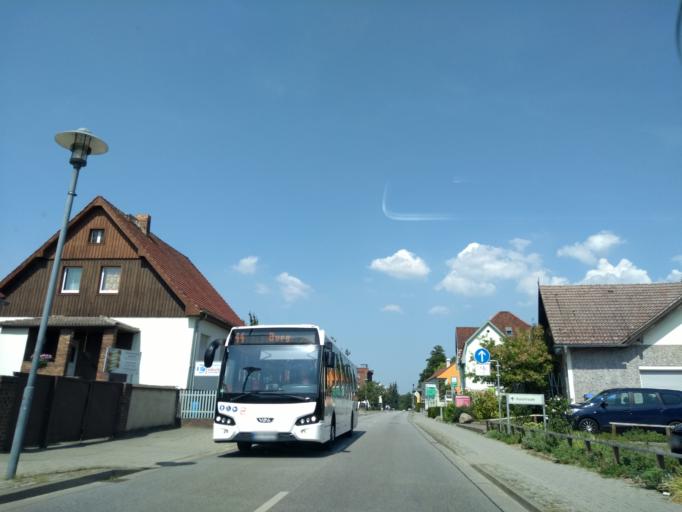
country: DE
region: Brandenburg
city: Burg
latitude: 51.8356
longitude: 14.1485
